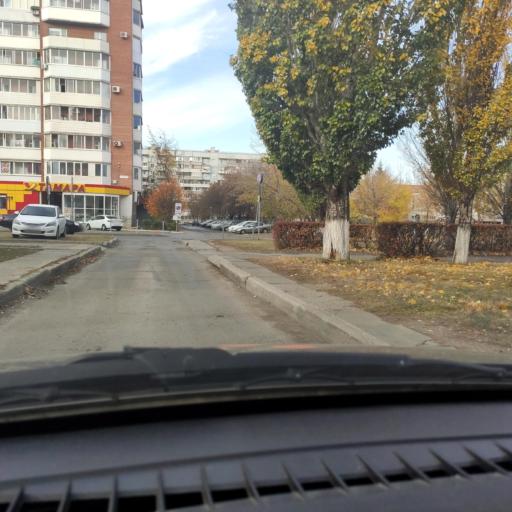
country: RU
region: Samara
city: Tol'yatti
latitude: 53.5347
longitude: 49.3349
